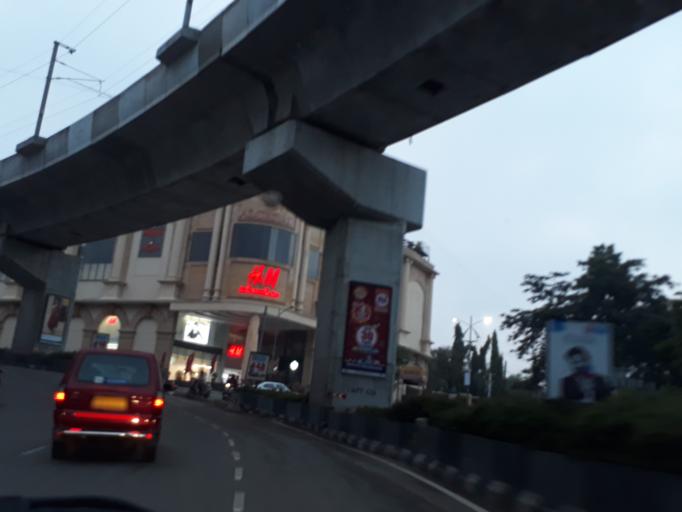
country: IN
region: Telangana
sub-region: Rangareddi
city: Kukatpalli
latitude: 17.4322
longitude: 78.4070
